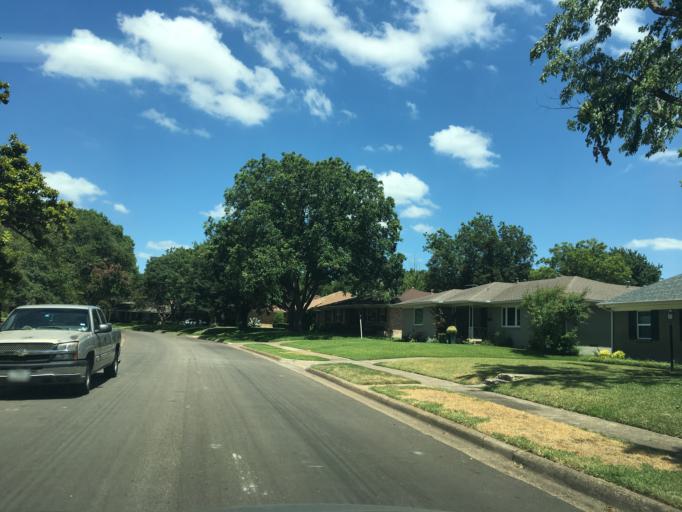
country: US
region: Texas
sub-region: Dallas County
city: Garland
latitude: 32.8497
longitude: -96.6928
